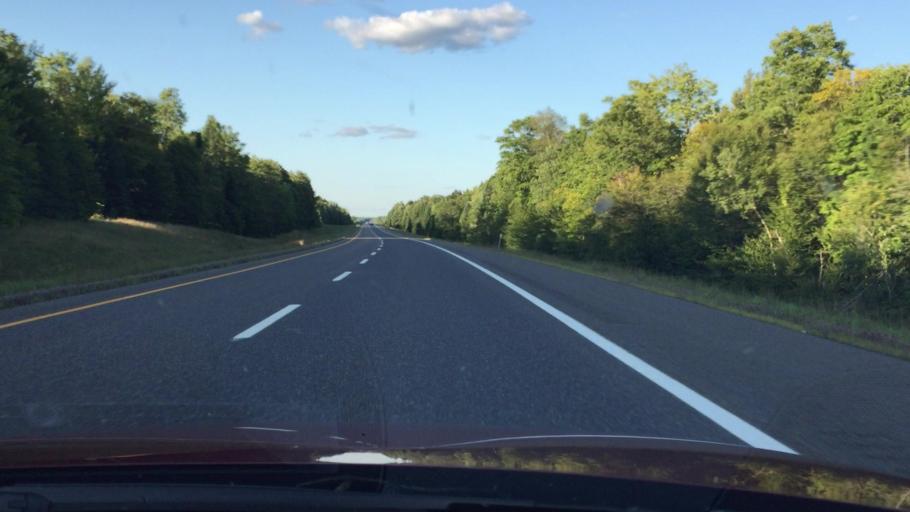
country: US
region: Maine
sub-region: Penobscot County
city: Patten
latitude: 46.0523
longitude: -68.2412
